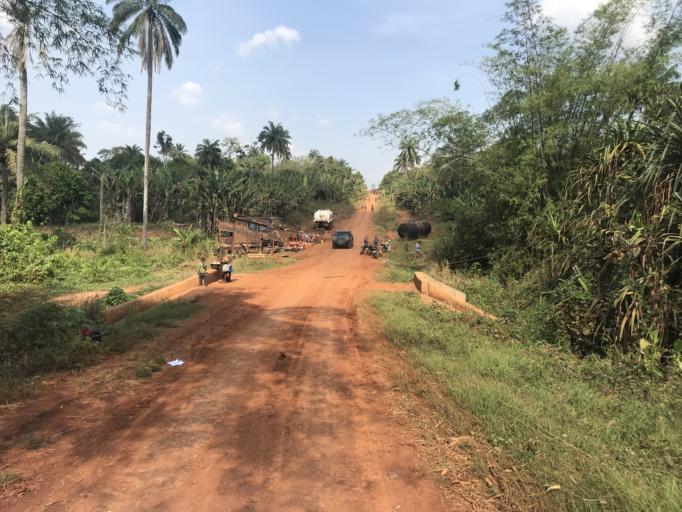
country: NG
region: Osun
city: Osu
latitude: 7.6489
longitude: 4.6627
